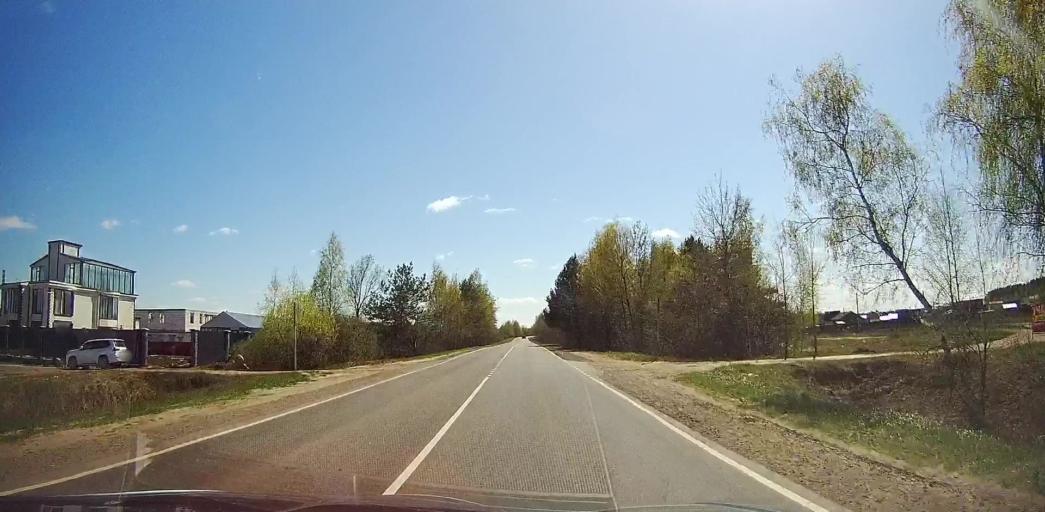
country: RU
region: Moskovskaya
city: Beloozerskiy
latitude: 55.5255
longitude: 38.4324
